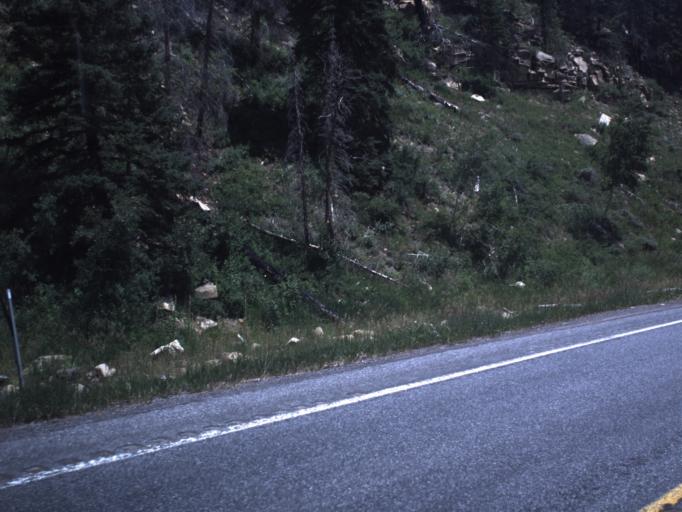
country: US
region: Utah
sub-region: Sanpete County
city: Fairview
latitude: 39.5823
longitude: -111.1898
